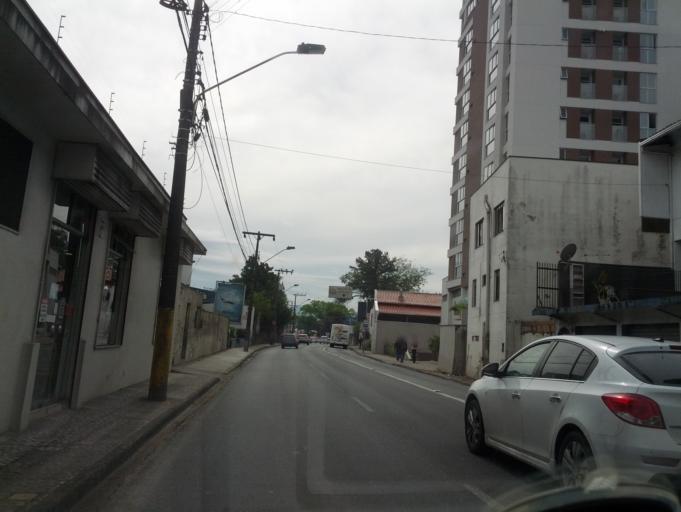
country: BR
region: Santa Catarina
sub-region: Blumenau
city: Blumenau
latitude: -26.9028
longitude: -49.0774
